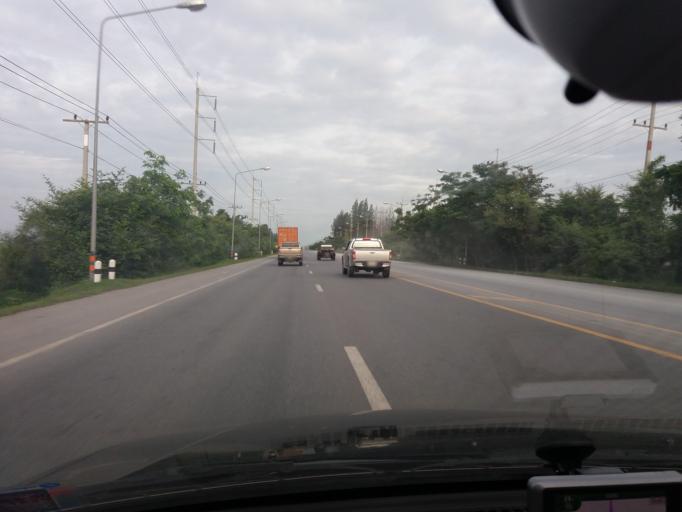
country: TH
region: Suphan Buri
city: U Thong
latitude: 14.3372
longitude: 99.8305
